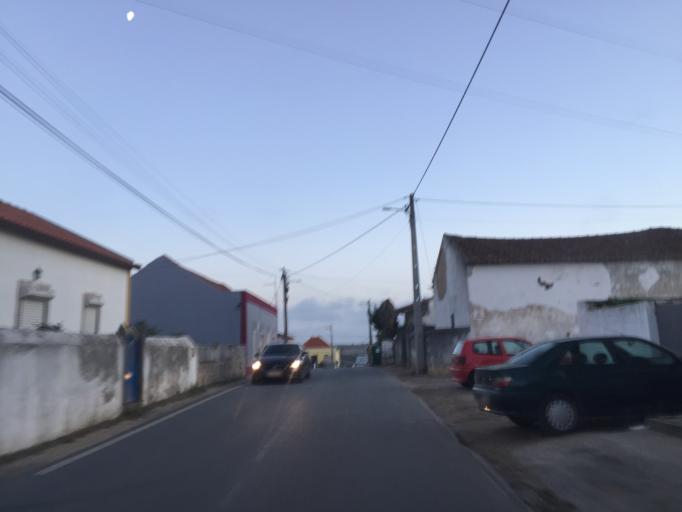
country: PT
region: Leiria
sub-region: Bombarral
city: Bombarral
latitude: 39.2807
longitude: -9.1903
